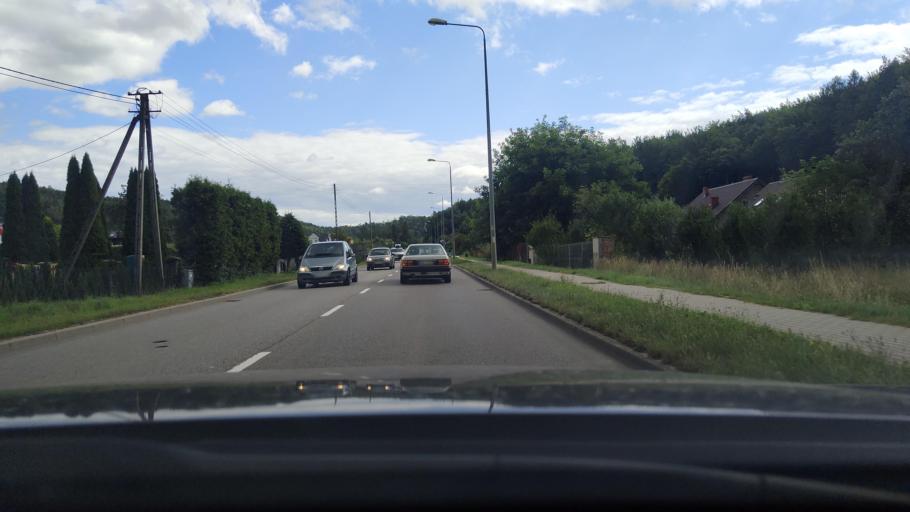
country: PL
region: Pomeranian Voivodeship
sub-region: Powiat wejherowski
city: Wejherowo
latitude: 54.5891
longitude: 18.2450
